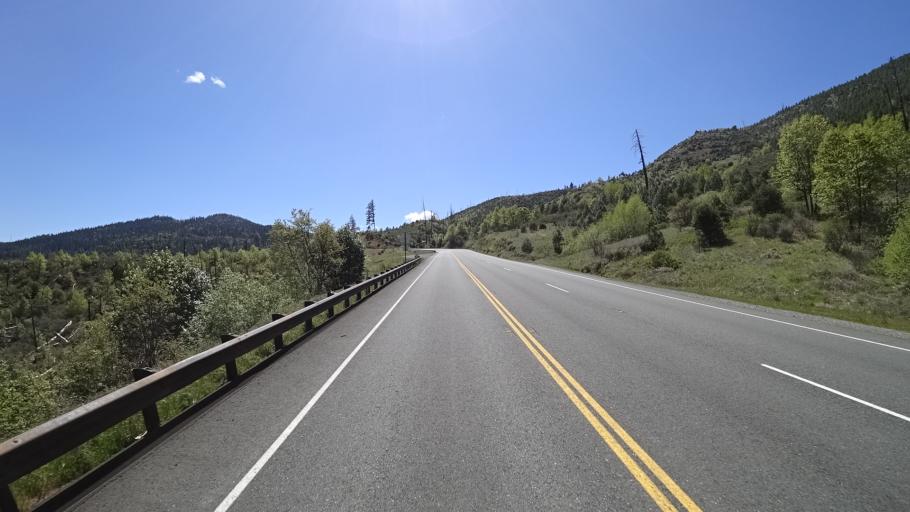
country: US
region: California
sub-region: Trinity County
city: Weaverville
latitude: 40.7453
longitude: -122.9747
